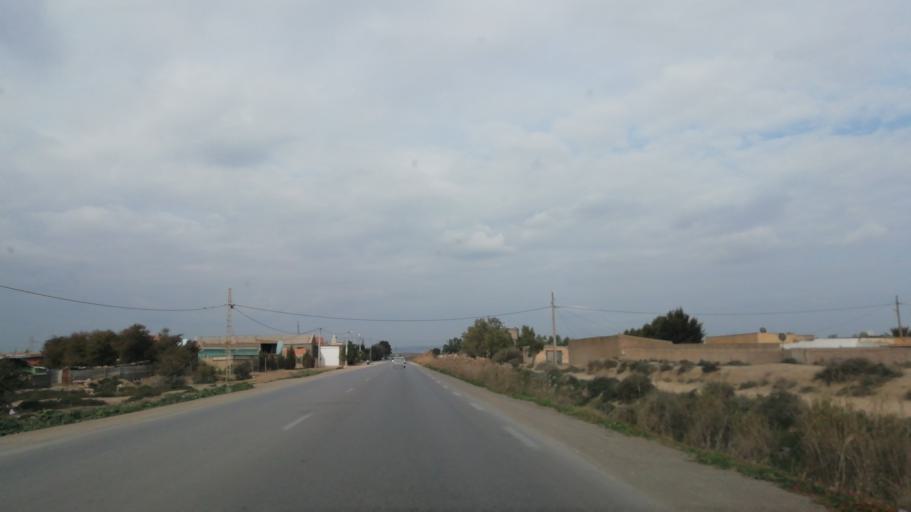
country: DZ
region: Mostaganem
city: Mostaganem
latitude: 35.6955
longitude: 0.0556
